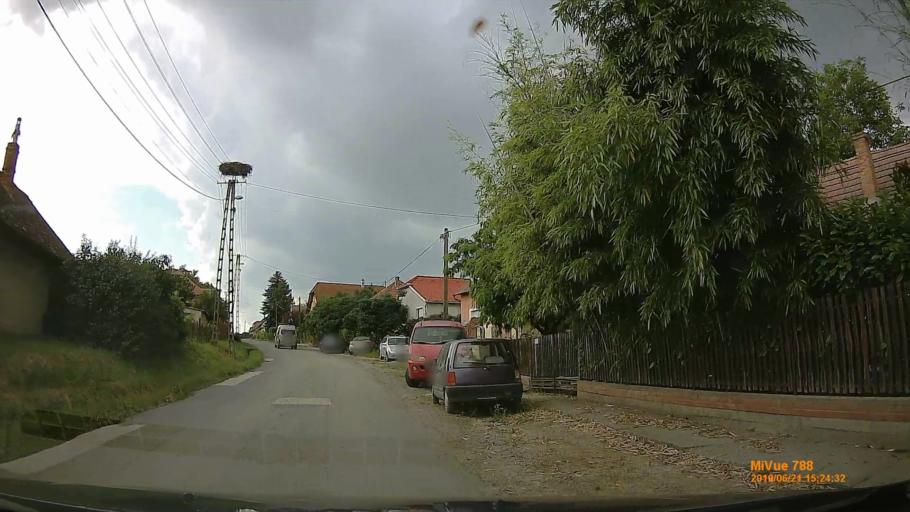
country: HU
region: Baranya
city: Kozarmisleny
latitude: 46.0436
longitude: 18.2537
